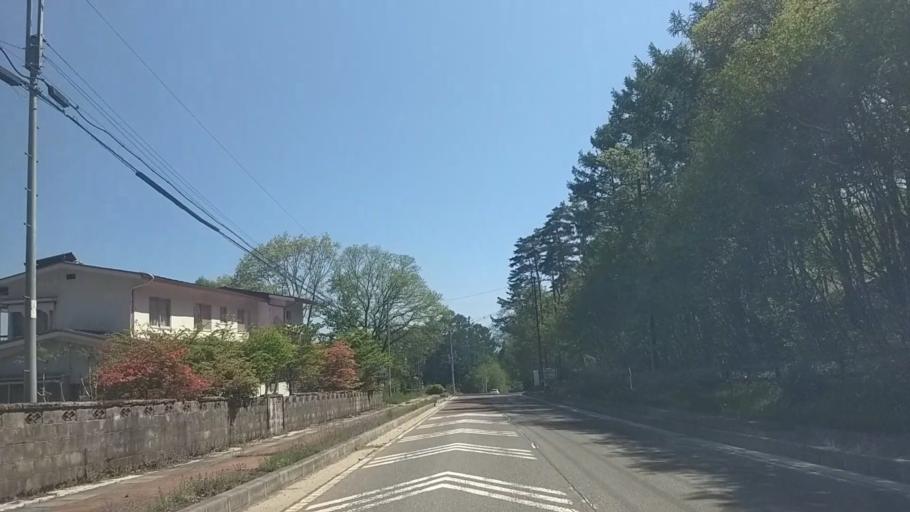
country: JP
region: Yamanashi
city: Nirasaki
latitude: 35.9128
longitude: 138.4330
